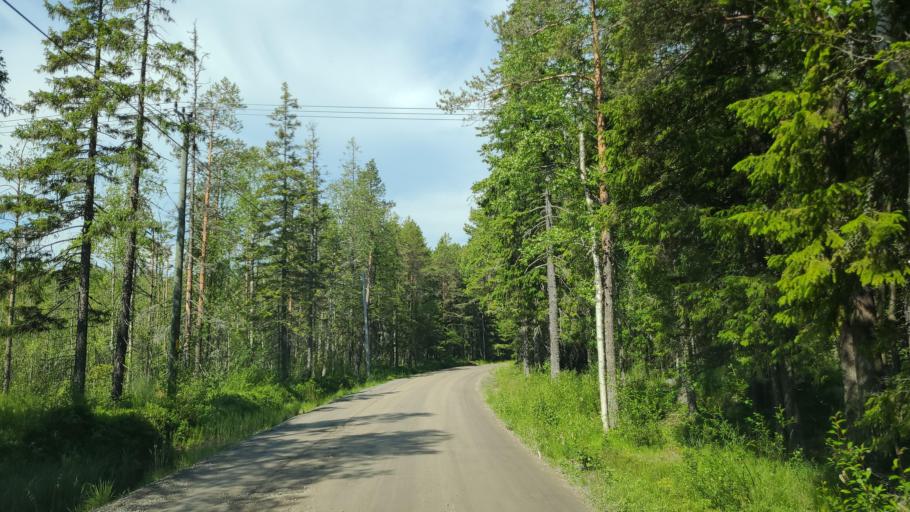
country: SE
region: Vaesterbotten
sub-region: Robertsfors Kommun
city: Robertsfors
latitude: 64.1456
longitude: 20.9577
